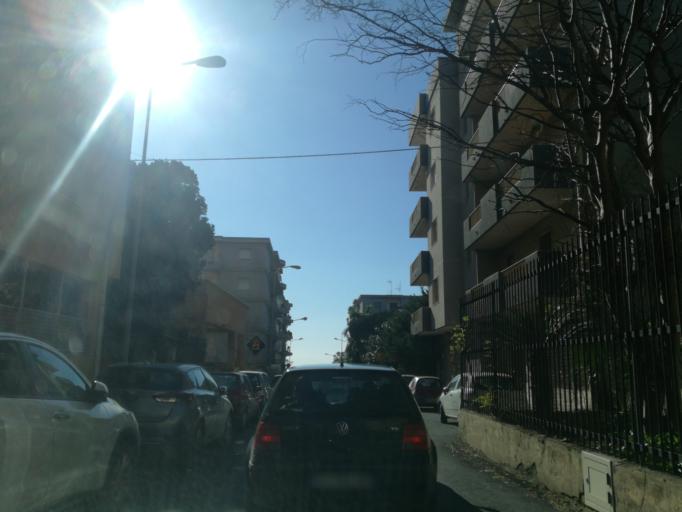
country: IT
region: Sicily
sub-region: Provincia di Caltanissetta
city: Gela
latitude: 37.0739
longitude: 14.2280
